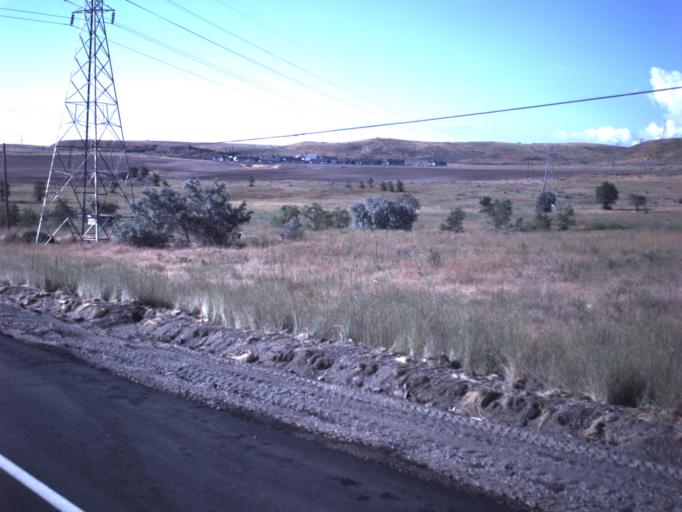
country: US
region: Utah
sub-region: Salt Lake County
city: Oquirrh
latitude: 40.6430
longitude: -112.0640
